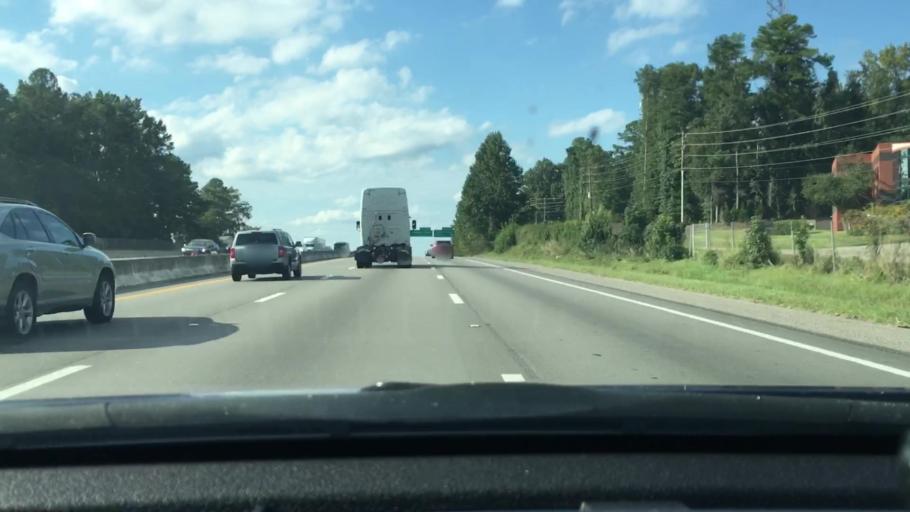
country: US
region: South Carolina
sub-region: Lexington County
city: Seven Oaks
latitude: 34.0624
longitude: -81.1370
